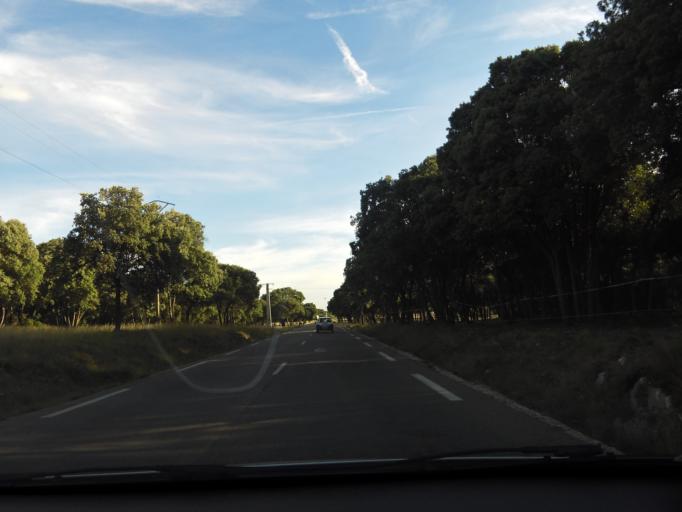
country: FR
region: Languedoc-Roussillon
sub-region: Departement de l'Herault
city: Saint-Mathieu-de-Treviers
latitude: 43.7781
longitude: 3.8710
